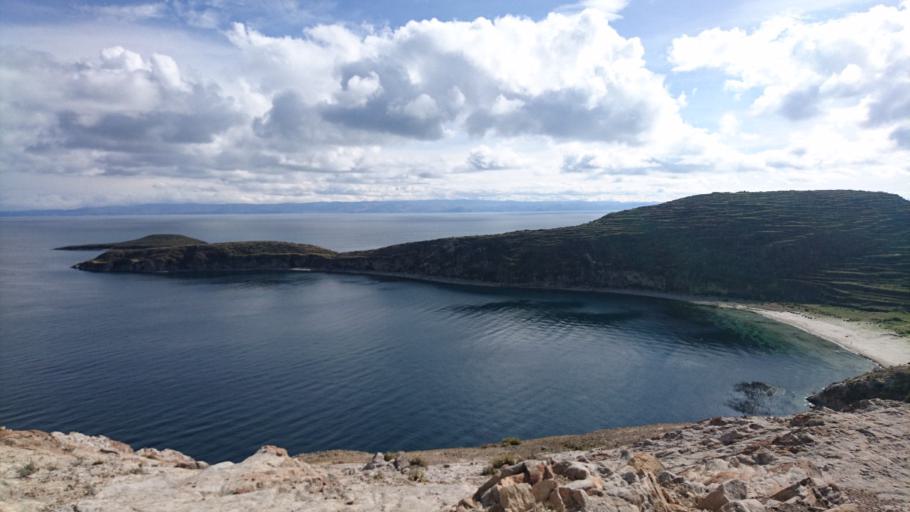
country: BO
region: La Paz
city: Yumani
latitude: -15.9901
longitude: -69.1981
